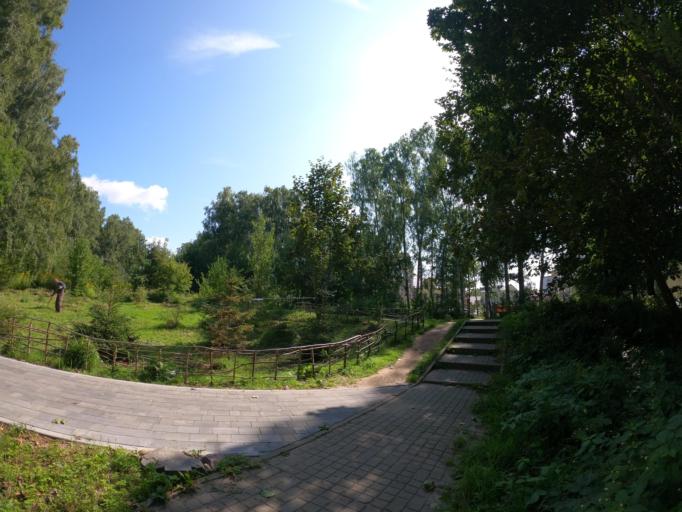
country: RU
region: Kaliningrad
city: Otradnoye
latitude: 54.9401
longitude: 20.1292
